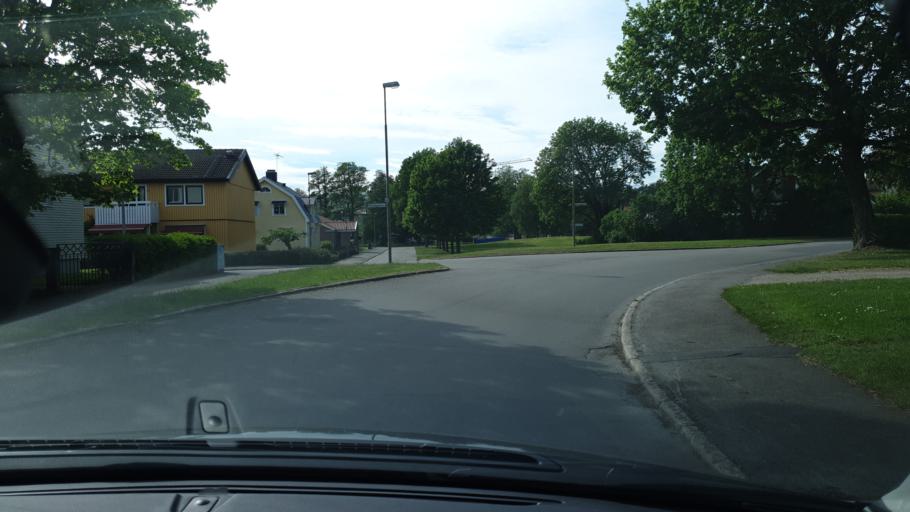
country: SE
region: Joenkoeping
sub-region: Vetlanda Kommun
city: Vetlanda
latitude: 57.4283
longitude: 15.0910
